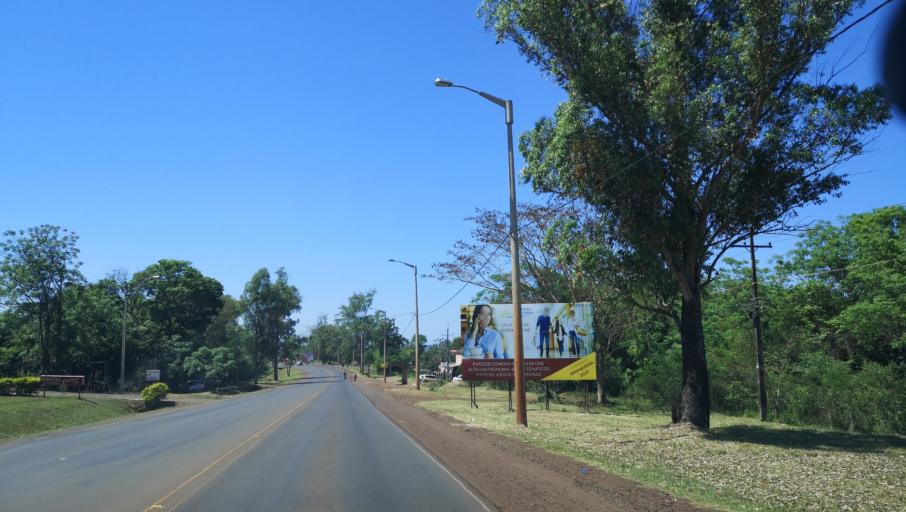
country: PY
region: Itapua
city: San Juan del Parana
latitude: -27.2904
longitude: -55.9354
